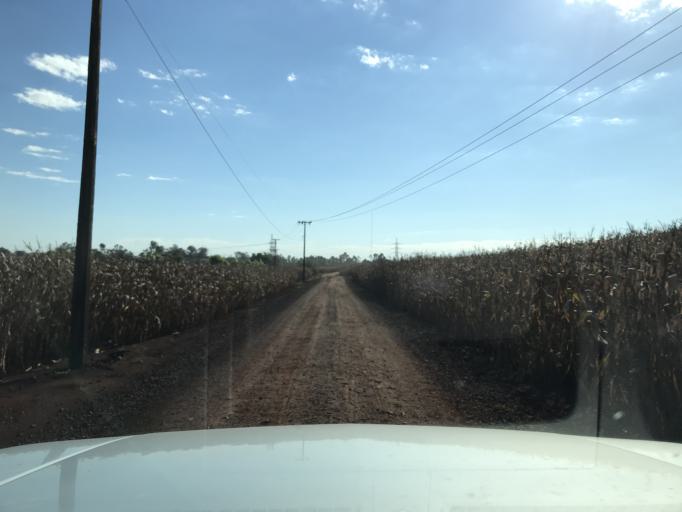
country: BR
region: Parana
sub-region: Palotina
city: Palotina
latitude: -24.2763
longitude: -53.8194
